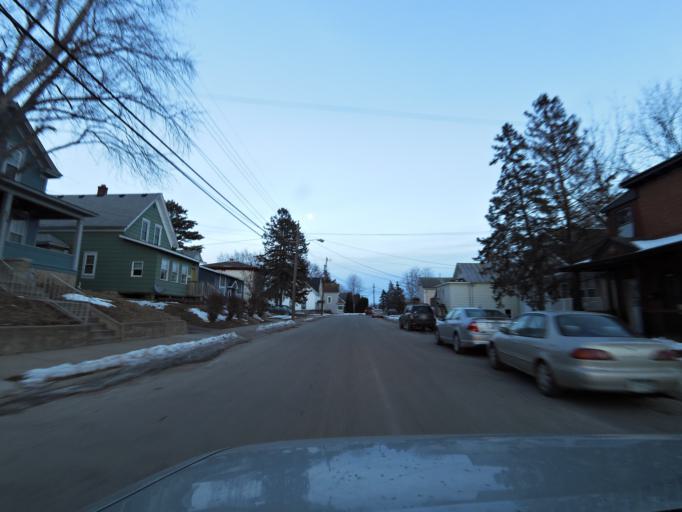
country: US
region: Minnesota
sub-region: Washington County
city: Stillwater
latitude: 45.0602
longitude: -92.8156
